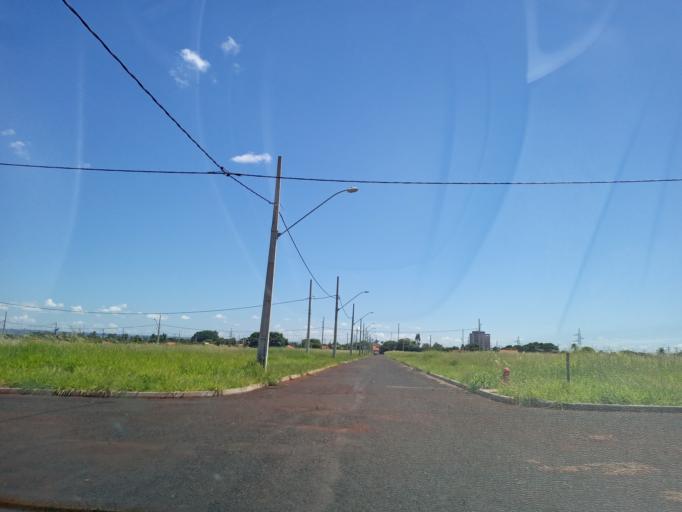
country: BR
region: Minas Gerais
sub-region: Centralina
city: Centralina
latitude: -18.5978
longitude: -49.1972
